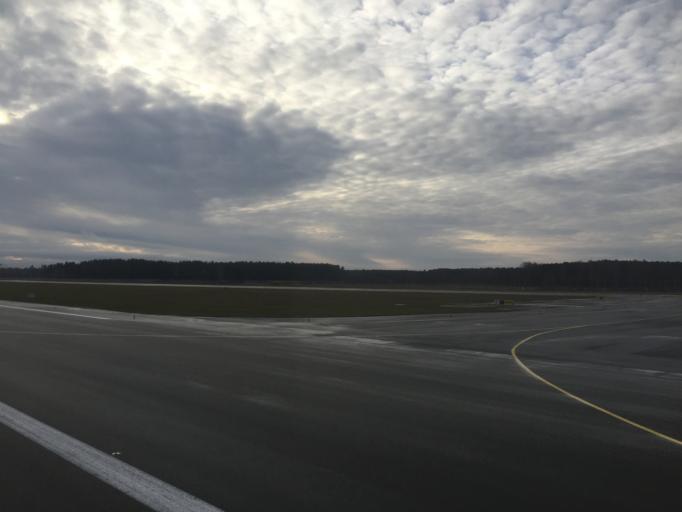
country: LV
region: Babite
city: Pinki
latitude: 56.9175
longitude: 23.9702
